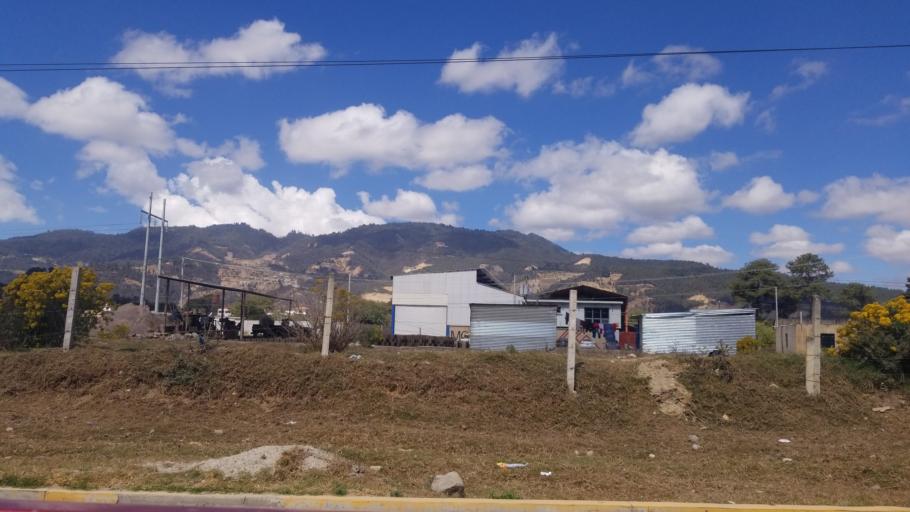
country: GT
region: Quetzaltenango
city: Quetzaltenango
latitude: 14.8182
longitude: -91.5365
